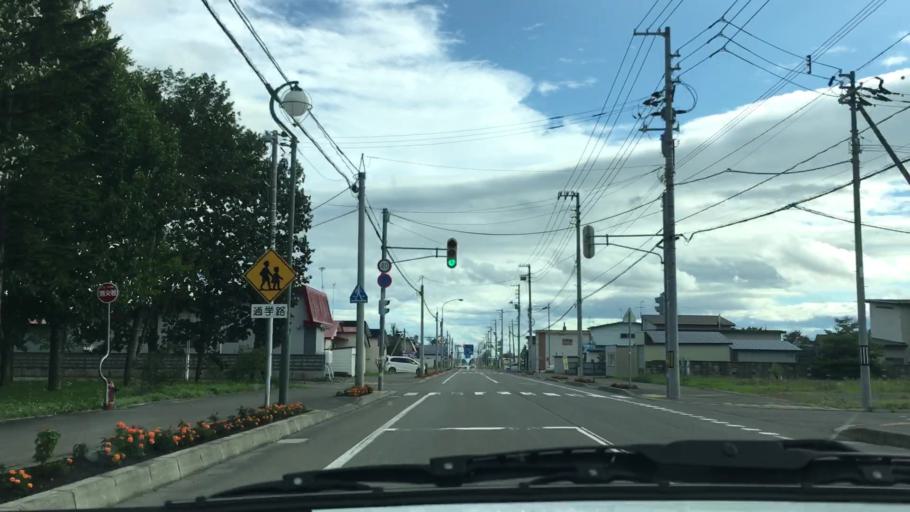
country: JP
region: Hokkaido
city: Otofuke
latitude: 43.2310
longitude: 143.2948
